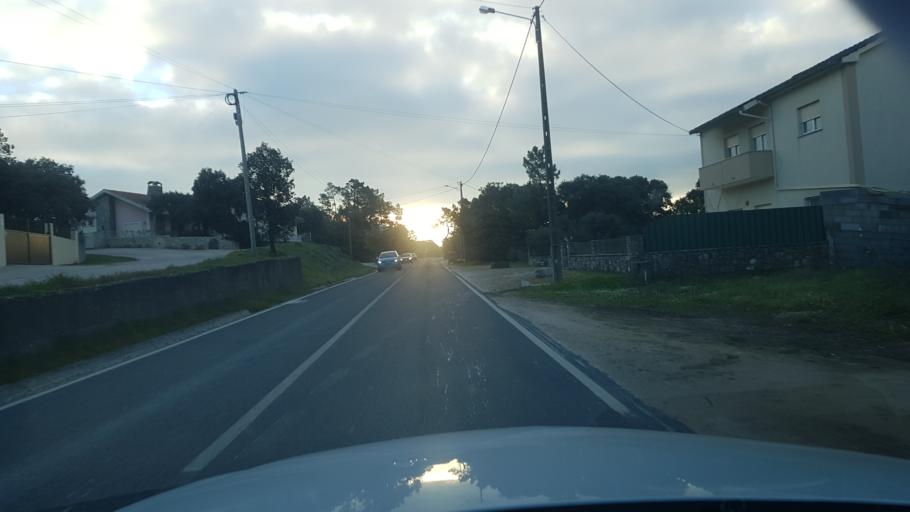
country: PT
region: Santarem
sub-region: Ourem
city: Fatima
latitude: 39.5985
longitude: -8.6458
